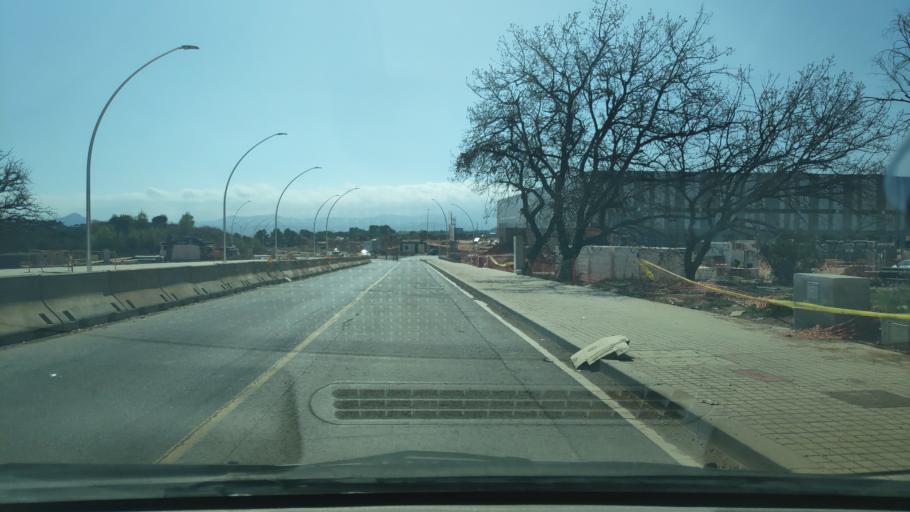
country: ES
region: Catalonia
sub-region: Provincia de Barcelona
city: Barbera del Valles
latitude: 41.5339
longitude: 2.1331
